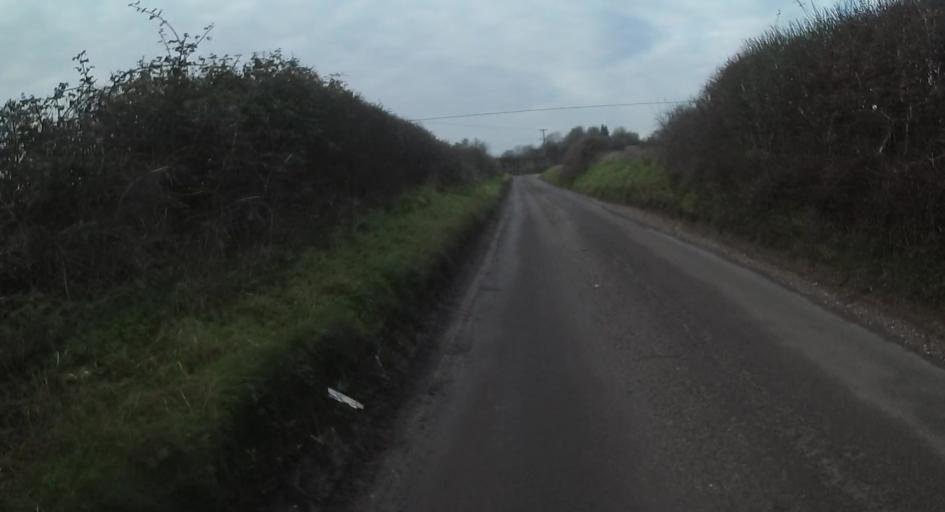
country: GB
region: England
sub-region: Hampshire
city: Tadley
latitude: 51.2850
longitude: -1.1648
